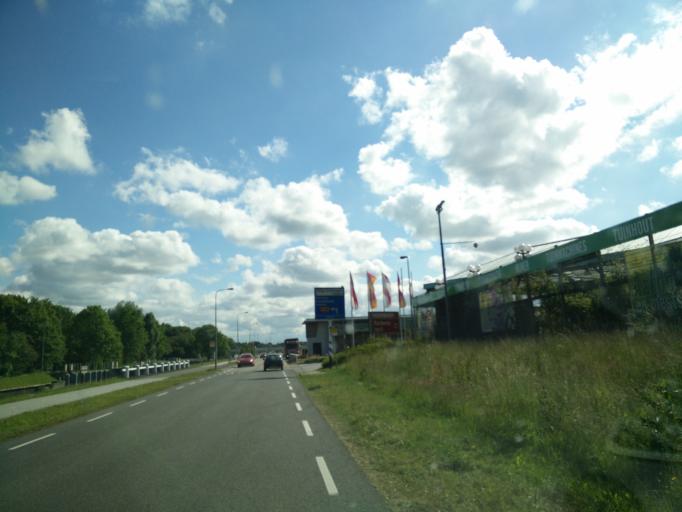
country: NL
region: Groningen
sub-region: Gemeente Groningen
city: Korrewegwijk
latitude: 53.2513
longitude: 6.5818
